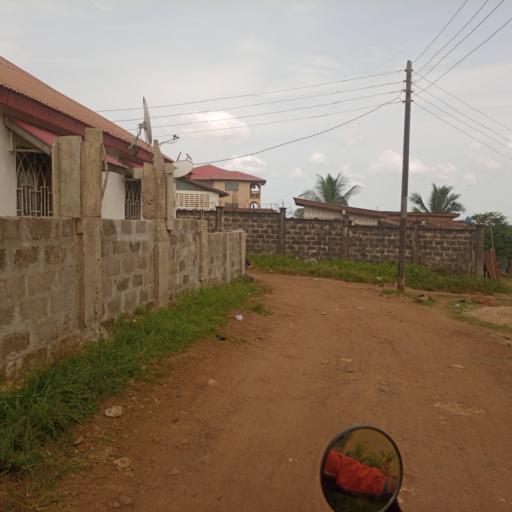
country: SL
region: Western Area
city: Hastings
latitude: 8.3942
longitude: -13.1421
